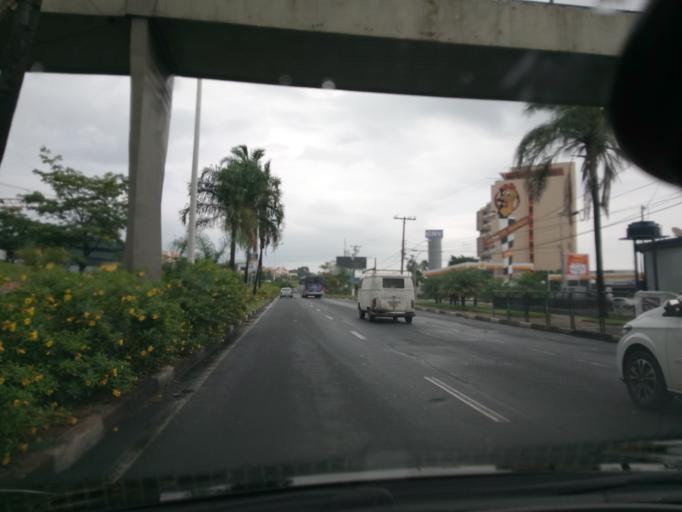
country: BR
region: Sao Paulo
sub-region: Campinas
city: Campinas
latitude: -22.9297
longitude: -47.0699
